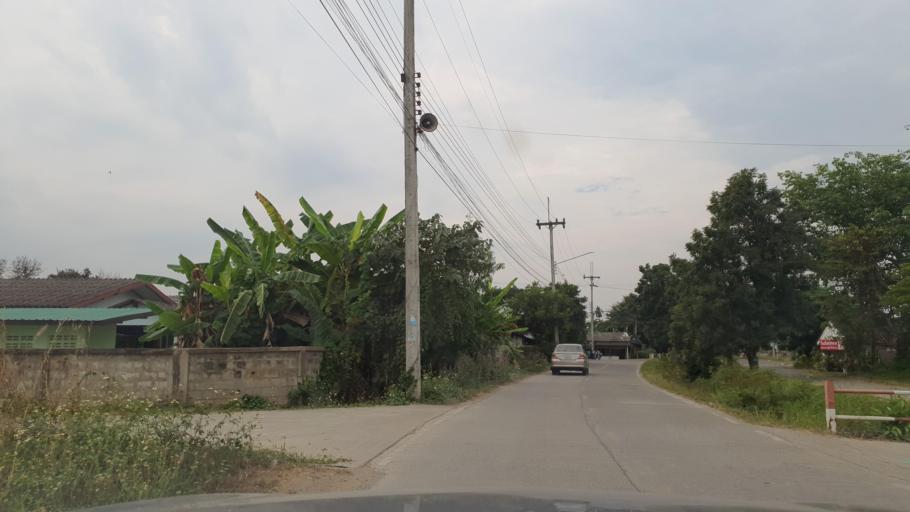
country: TH
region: Chiang Mai
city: Hang Dong
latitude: 18.6861
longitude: 98.9343
